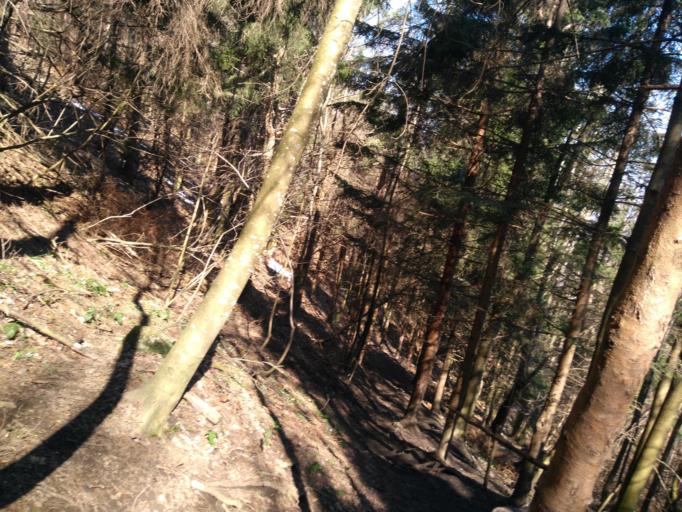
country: HR
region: Varazdinska
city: Ivanec
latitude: 46.1853
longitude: 16.1099
